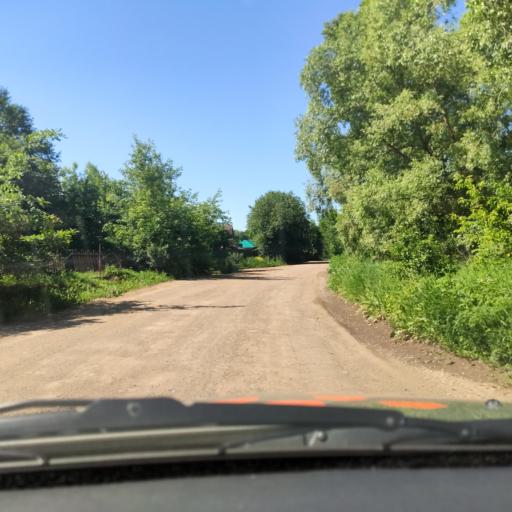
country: RU
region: Bashkortostan
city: Iglino
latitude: 54.7878
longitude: 56.1923
